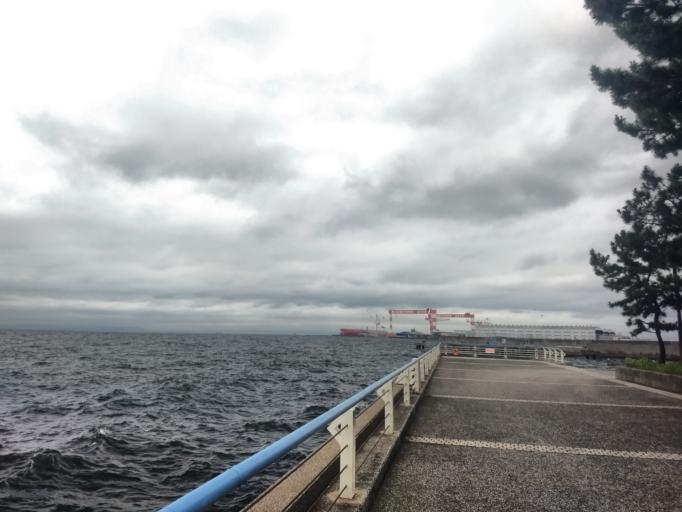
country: JP
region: Kanagawa
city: Yokosuka
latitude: 35.3380
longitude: 139.6486
